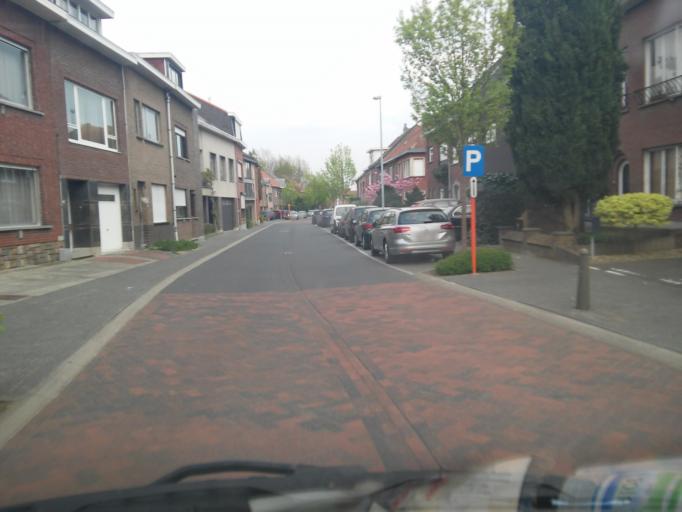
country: BE
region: Flanders
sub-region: Provincie Antwerpen
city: Mechelen
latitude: 51.0236
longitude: 4.4620
